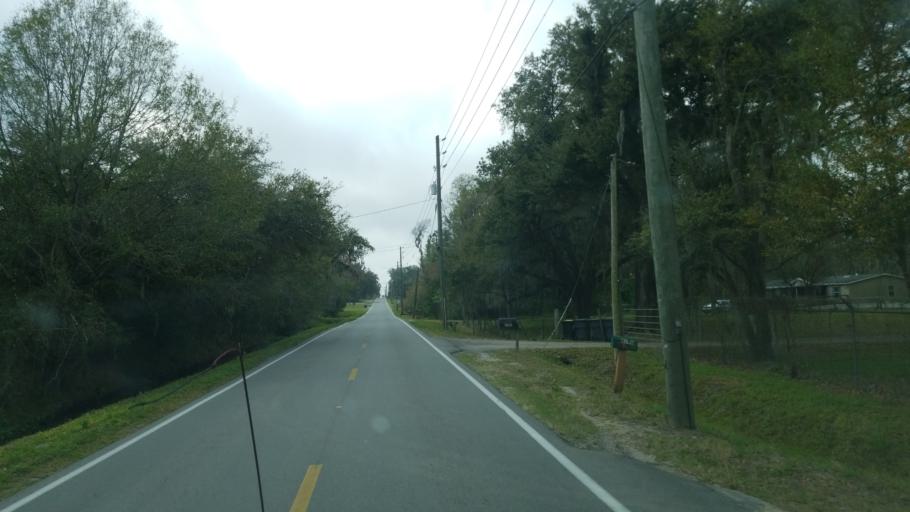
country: US
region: Florida
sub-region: Polk County
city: Kathleen
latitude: 28.1494
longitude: -82.0233
